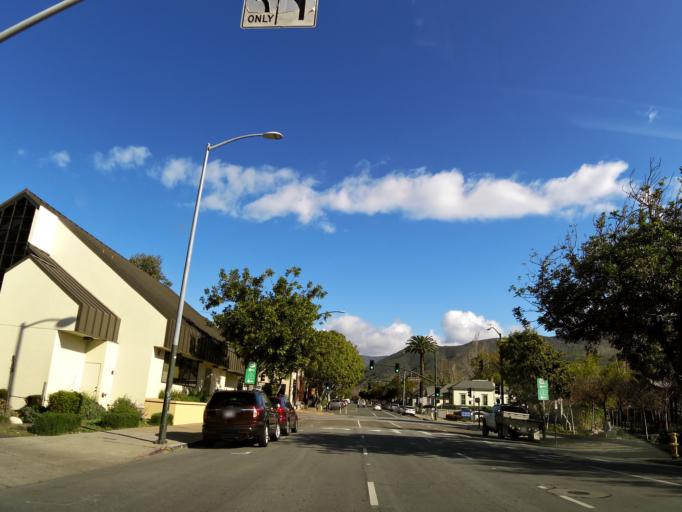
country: US
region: California
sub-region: San Luis Obispo County
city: San Luis Obispo
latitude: 35.2808
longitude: -120.6594
